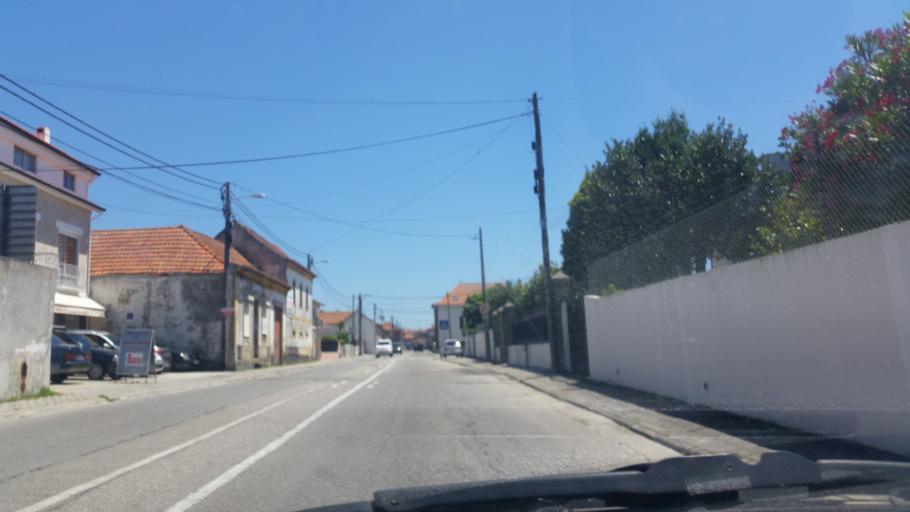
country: PT
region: Aveiro
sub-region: Aveiro
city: Aveiro
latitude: 40.6462
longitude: -8.6259
